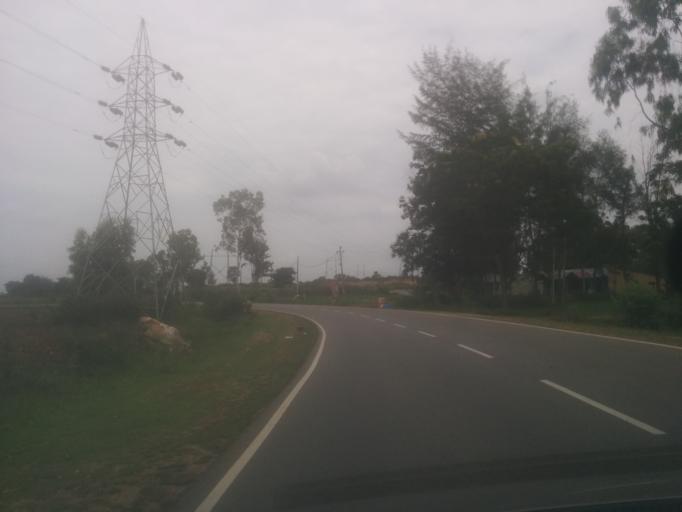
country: IN
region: Karnataka
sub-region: Hassan
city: Belur
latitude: 13.1629
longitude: 75.8950
